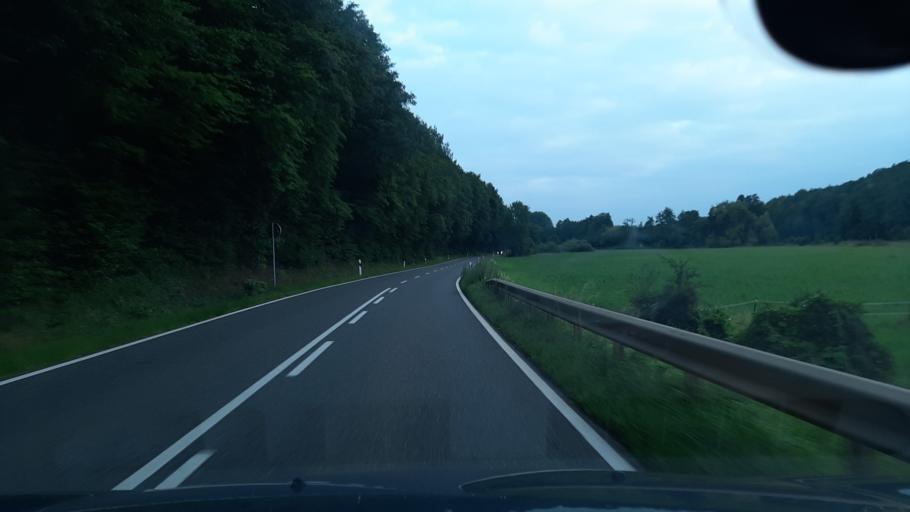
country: DE
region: North Rhine-Westphalia
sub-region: Regierungsbezirk Koln
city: Mechernich
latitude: 50.6131
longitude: 6.6991
